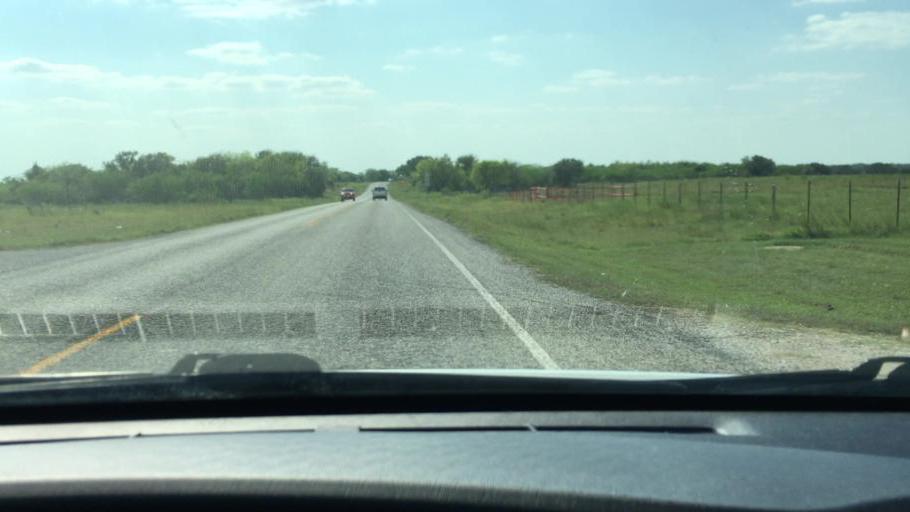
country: US
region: Texas
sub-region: DeWitt County
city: Yorktown
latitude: 28.9189
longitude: -97.3395
